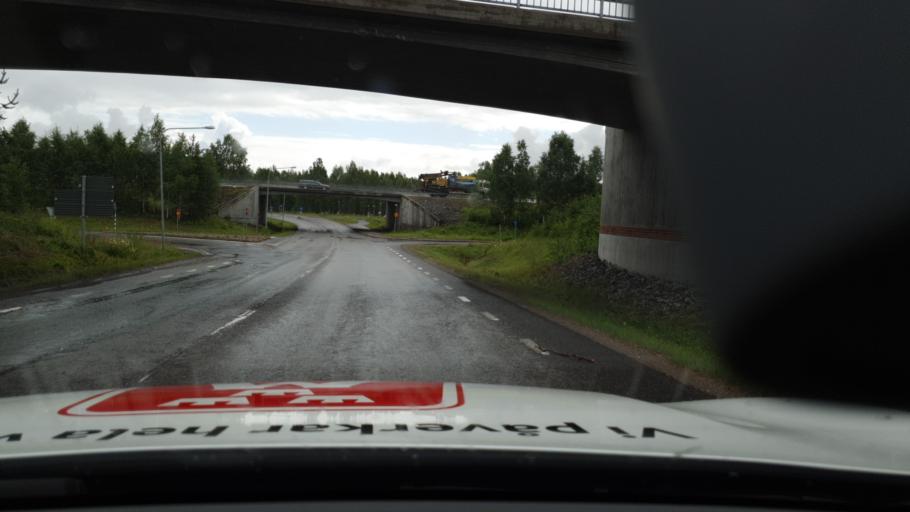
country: SE
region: Norrbotten
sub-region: Lulea Kommun
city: Sodra Sunderbyn
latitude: 65.5497
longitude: 21.8460
